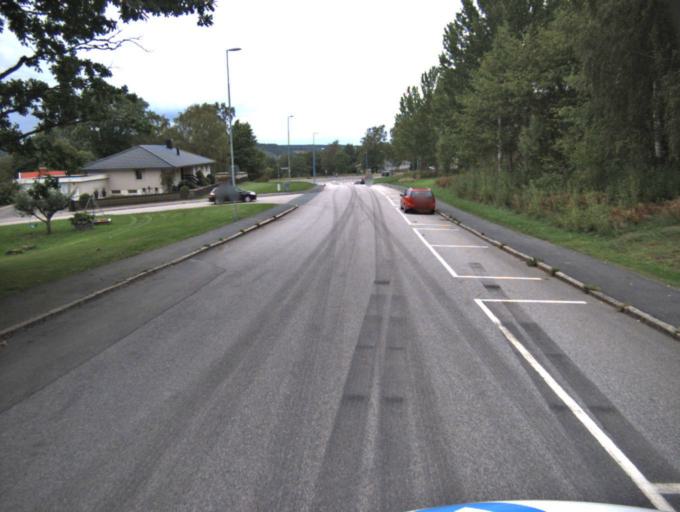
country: SE
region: Vaestra Goetaland
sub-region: Ulricehamns Kommun
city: Ulricehamn
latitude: 57.8018
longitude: 13.4330
